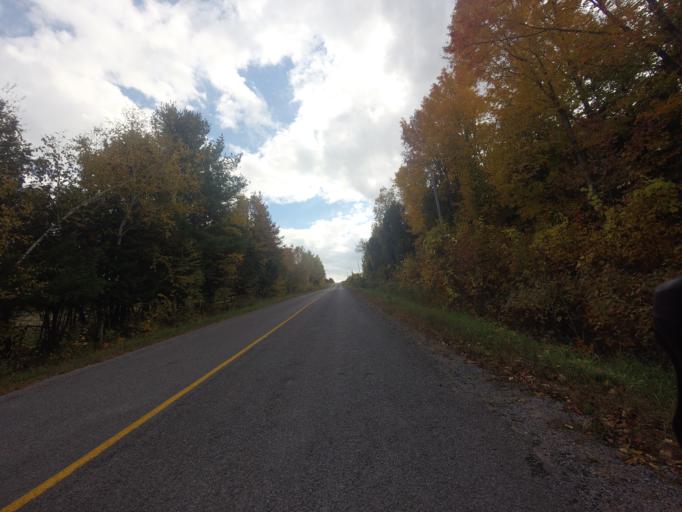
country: CA
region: Ontario
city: Pembroke
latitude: 45.5779
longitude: -77.1305
